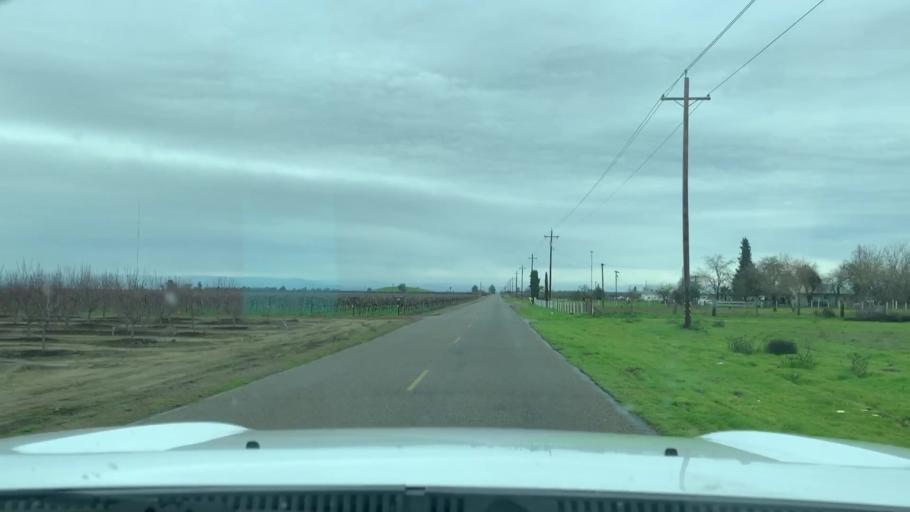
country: US
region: California
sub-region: Fresno County
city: Caruthers
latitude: 36.5474
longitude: -119.7691
